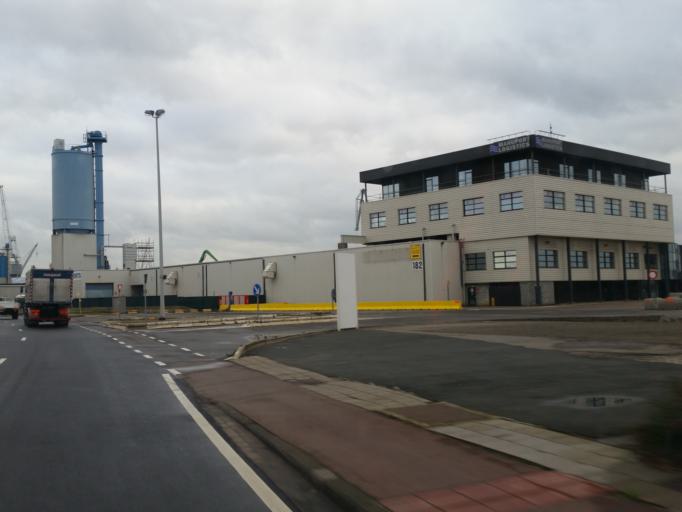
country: BE
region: Flanders
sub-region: Provincie Antwerpen
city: Antwerpen
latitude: 51.2612
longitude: 4.4031
